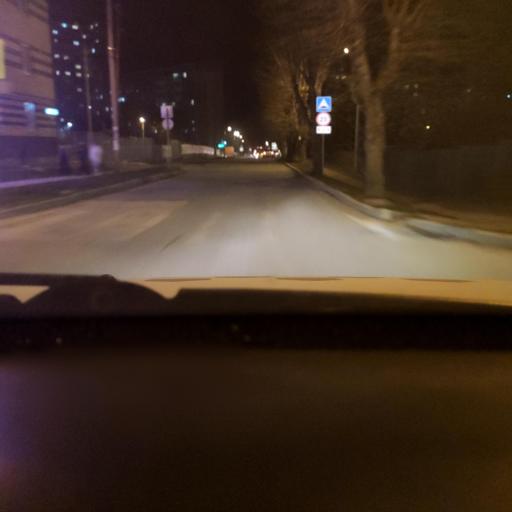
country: RU
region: Perm
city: Perm
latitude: 58.0304
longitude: 56.3104
